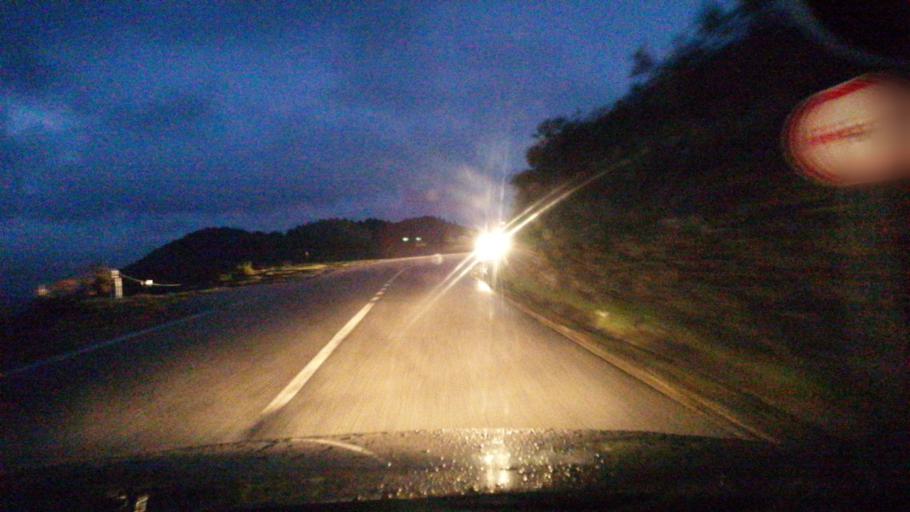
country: PT
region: Viseu
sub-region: Tabuaco
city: Tabuaco
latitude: 41.1462
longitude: -7.5411
